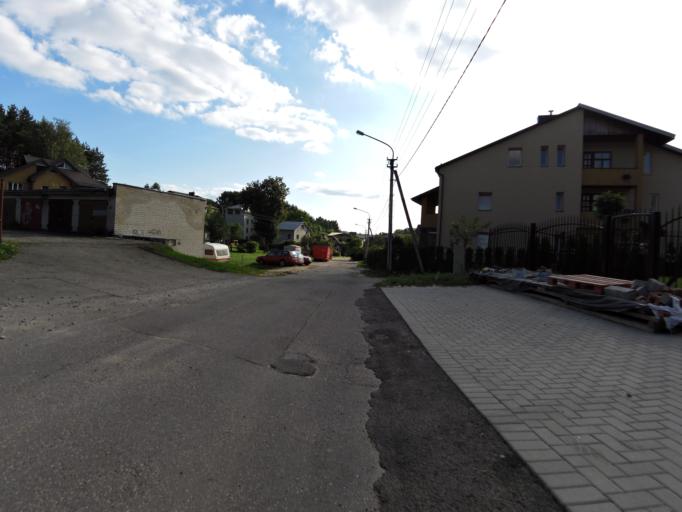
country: LT
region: Vilnius County
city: Rasos
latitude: 54.6879
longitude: 25.3182
